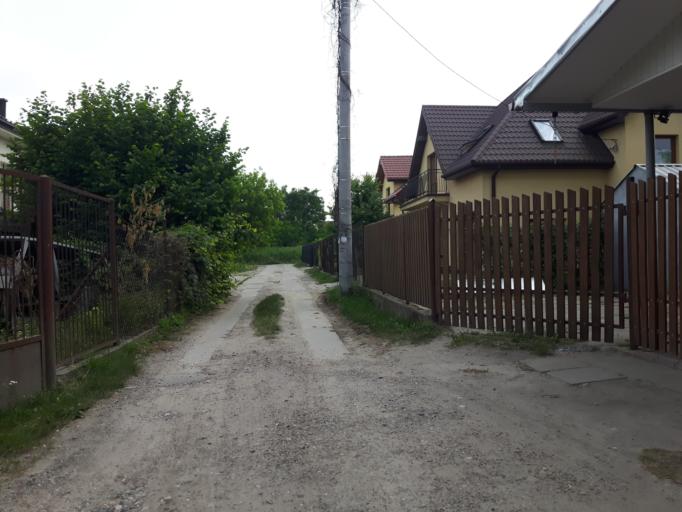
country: PL
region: Masovian Voivodeship
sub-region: Powiat wolominski
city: Zabki
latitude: 52.2818
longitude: 21.1194
